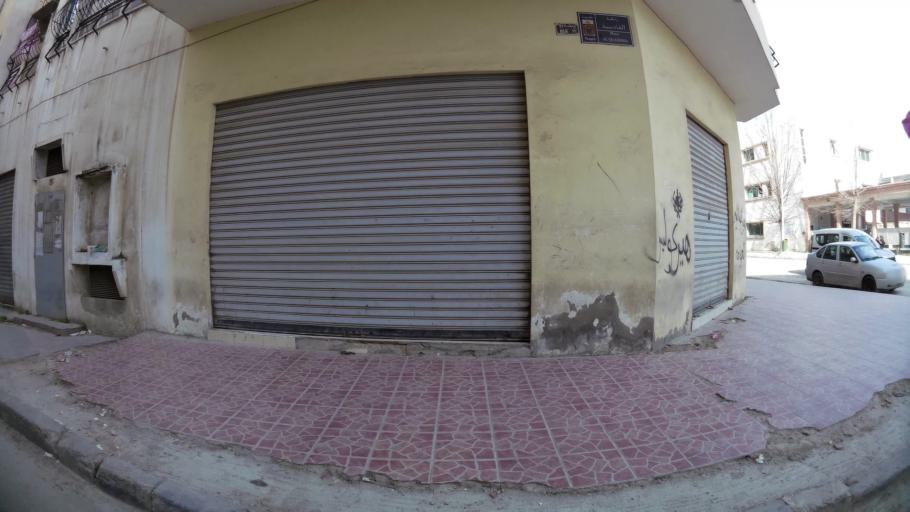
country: MA
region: Tanger-Tetouan
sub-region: Tanger-Assilah
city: Tangier
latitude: 35.7472
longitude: -5.7958
